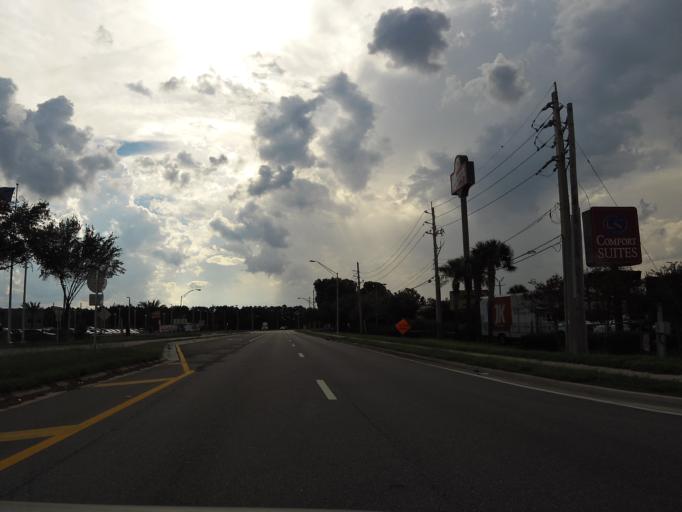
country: US
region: Florida
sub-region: Duval County
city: Jacksonville
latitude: 30.3358
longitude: -81.7622
